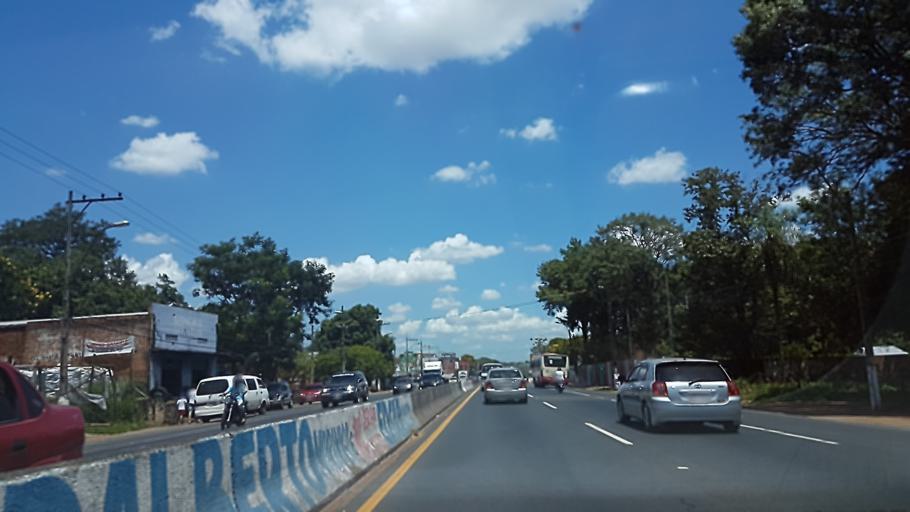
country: PY
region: Central
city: Capiata
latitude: -25.3470
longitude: -57.4724
